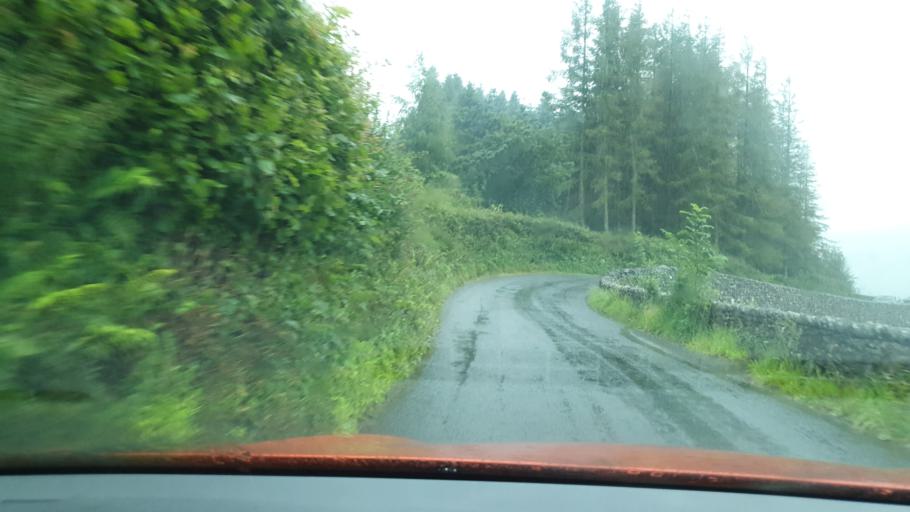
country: GB
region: England
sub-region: Cumbria
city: Millom
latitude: 54.3015
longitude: -3.2281
